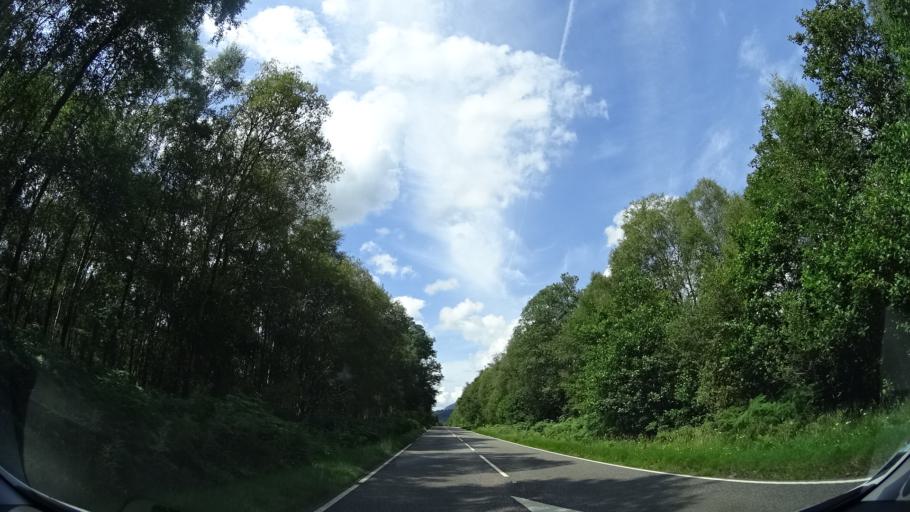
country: GB
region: Scotland
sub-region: Highland
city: Fort William
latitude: 56.8593
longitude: -5.3661
